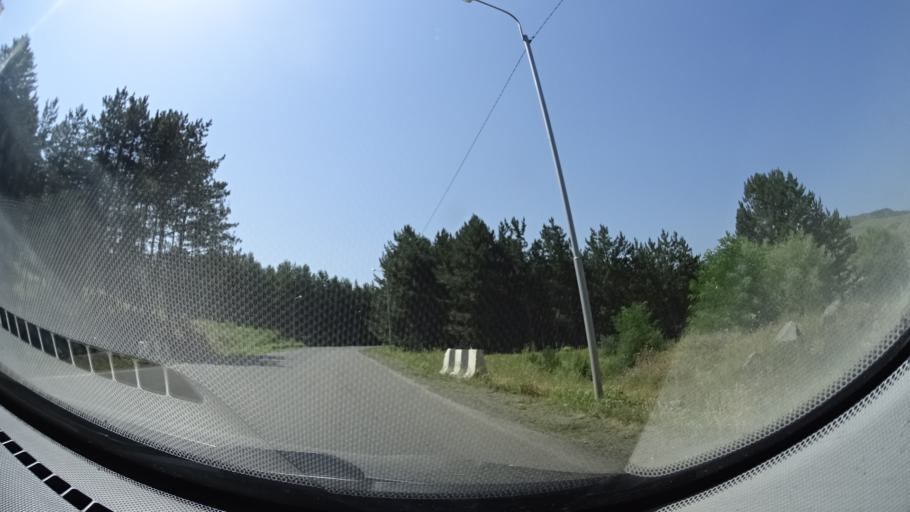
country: GE
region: Samtskhe-Javakheti
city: Aspindza
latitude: 41.5829
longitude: 43.2452
